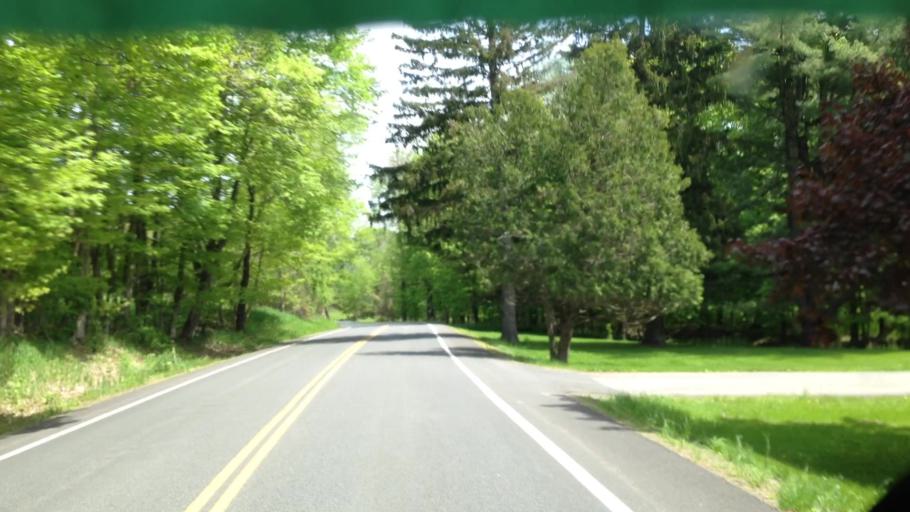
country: US
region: New York
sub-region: Dutchess County
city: Pine Plains
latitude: 42.0589
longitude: -73.6236
